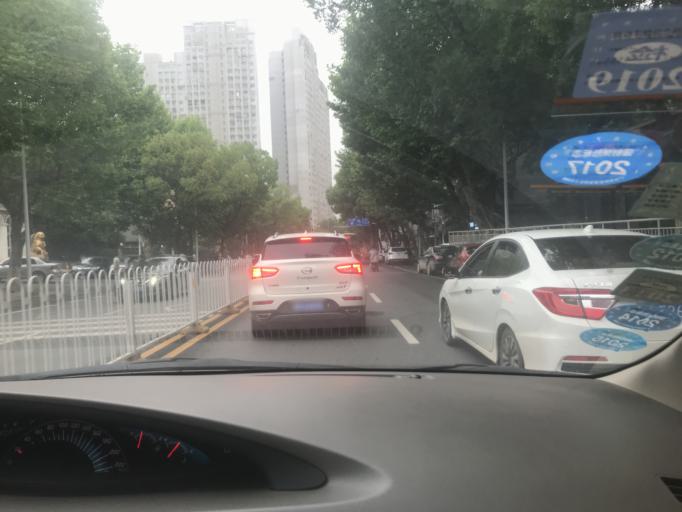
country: CN
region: Hubei
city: Wuhan
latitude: 30.5524
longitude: 114.2671
